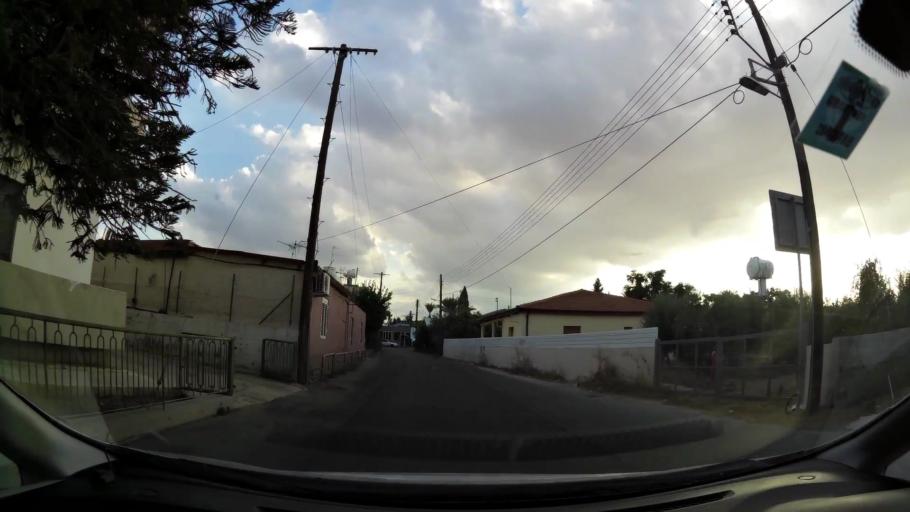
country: CY
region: Lefkosia
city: Tseri
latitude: 35.1180
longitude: 33.3122
